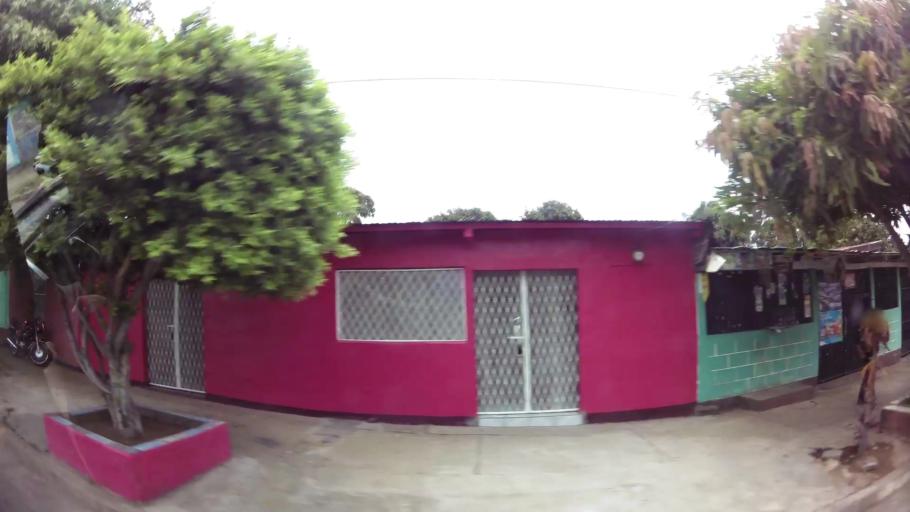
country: NI
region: Managua
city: Managua
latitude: 12.1172
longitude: -86.2360
